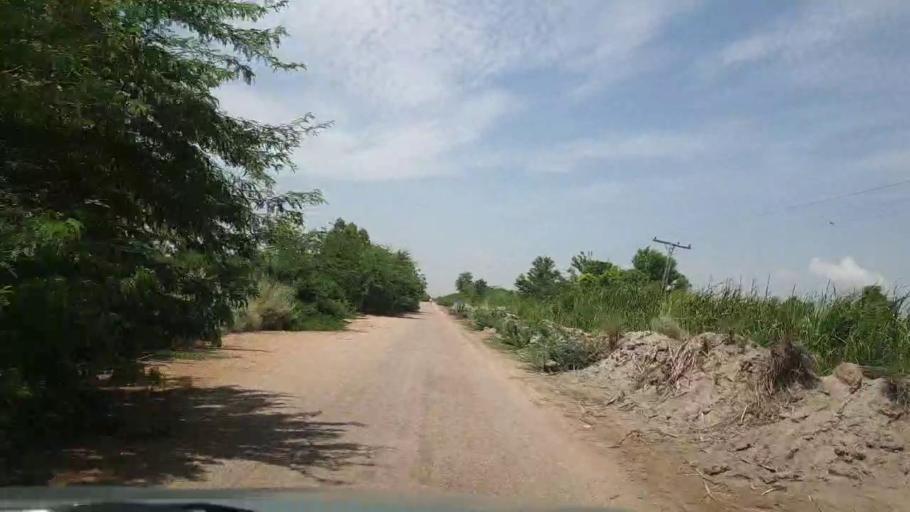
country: PK
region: Sindh
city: Bozdar
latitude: 27.0882
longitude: 68.9917
